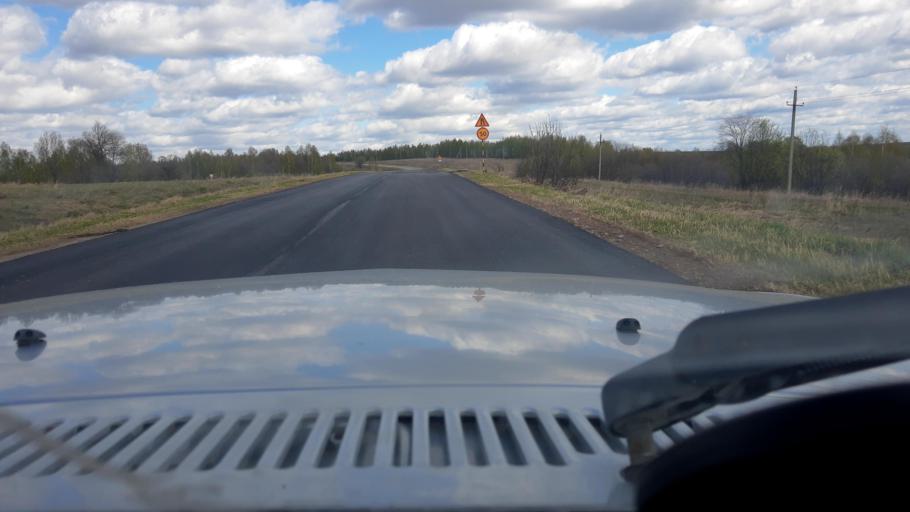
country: RU
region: Bashkortostan
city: Pavlovka
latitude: 55.3623
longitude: 56.4153
